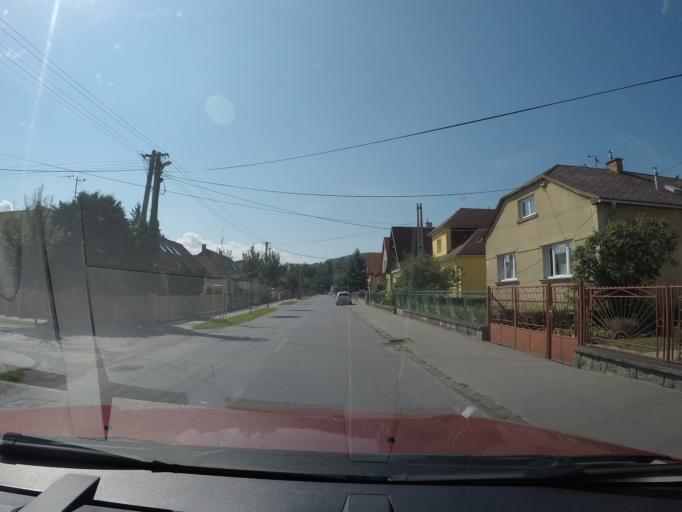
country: SK
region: Presovsky
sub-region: Okres Presov
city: Presov
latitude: 48.9940
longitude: 21.2236
